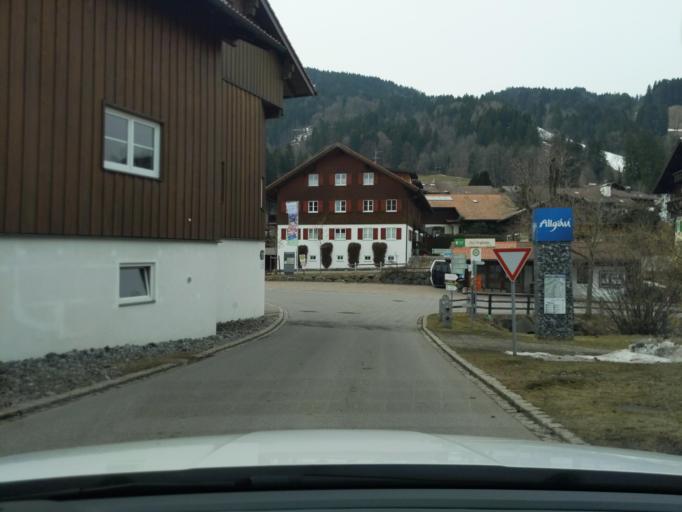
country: DE
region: Bavaria
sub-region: Swabia
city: Ofterschwang
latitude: 47.4955
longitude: 10.2362
